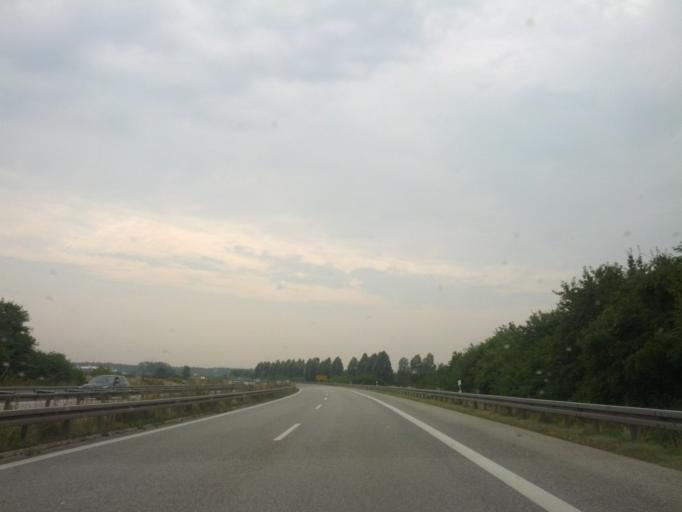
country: DE
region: Mecklenburg-Vorpommern
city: Stabelow
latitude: 54.0508
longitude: 12.0335
